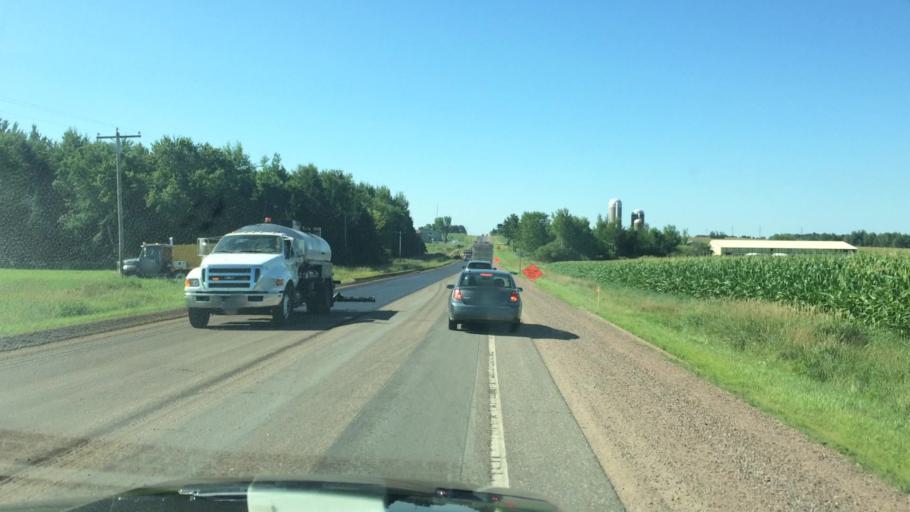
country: US
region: Wisconsin
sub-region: Marathon County
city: Stratford
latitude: 44.8976
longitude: -90.0788
